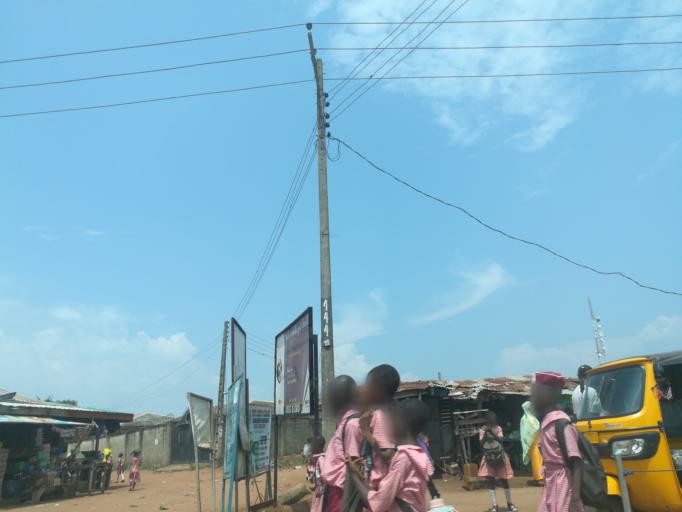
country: NG
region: Lagos
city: Ikorodu
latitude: 6.5775
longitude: 3.6284
